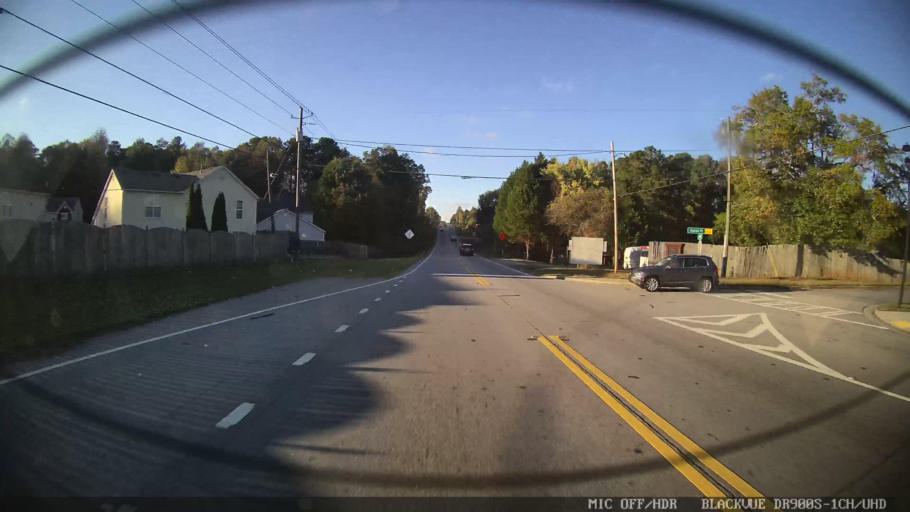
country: US
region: Georgia
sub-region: Clayton County
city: Lake City
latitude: 33.5981
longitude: -84.2973
